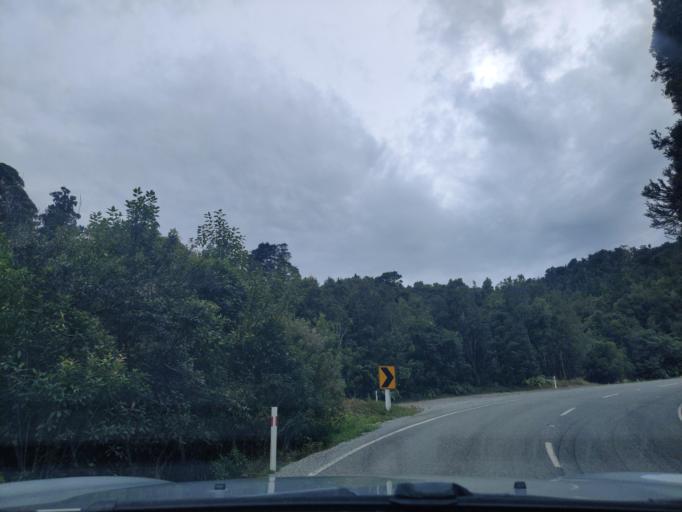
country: NZ
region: West Coast
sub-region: Westland District
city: Hokitika
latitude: -43.1748
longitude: 170.4567
